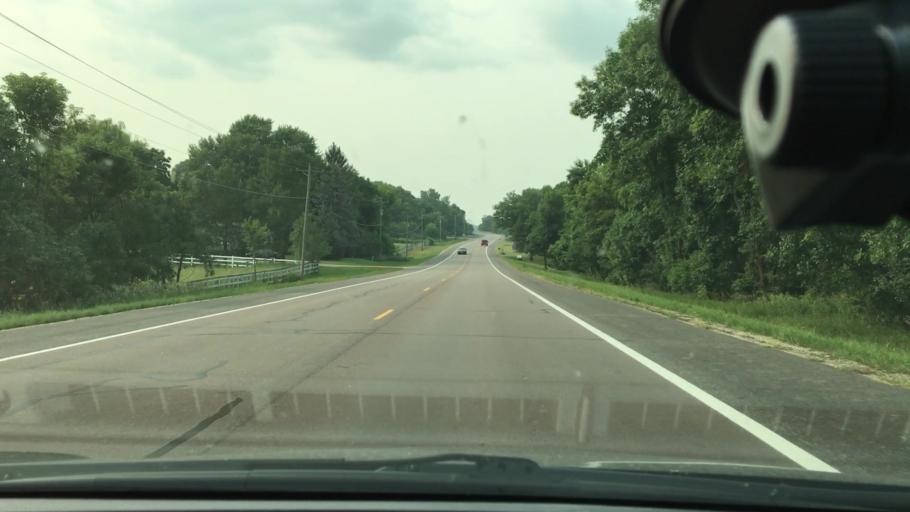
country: US
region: Minnesota
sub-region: Hennepin County
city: Dayton
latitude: 45.2493
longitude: -93.5348
